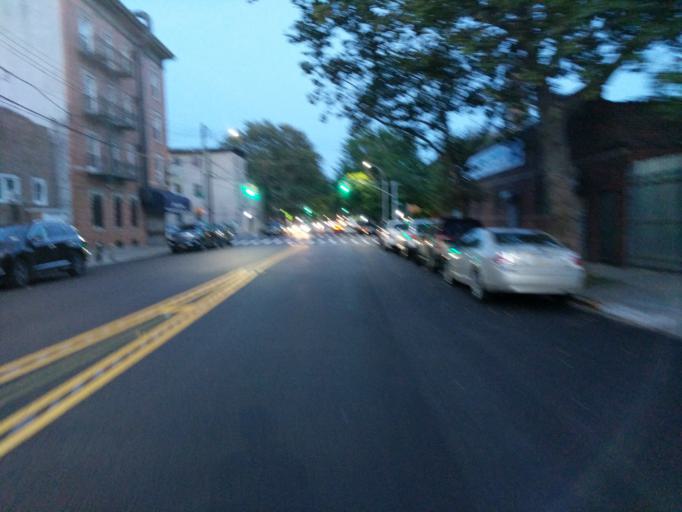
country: US
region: New York
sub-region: Queens County
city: Long Island City
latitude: 40.7613
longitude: -73.9406
